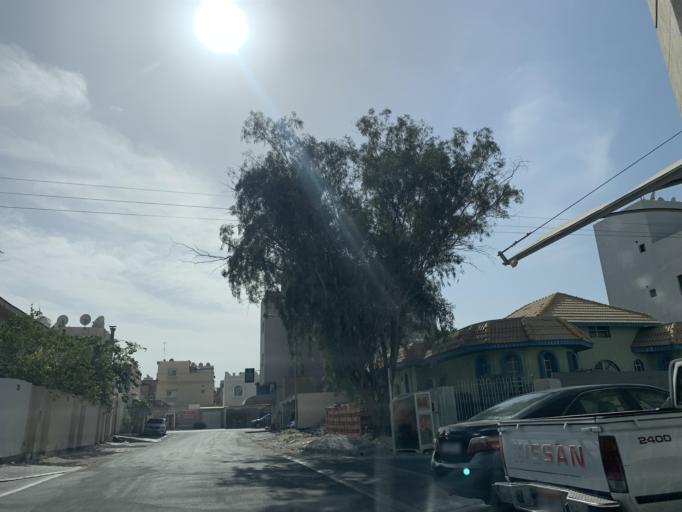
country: BH
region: Northern
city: Ar Rifa'
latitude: 26.1235
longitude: 50.5800
